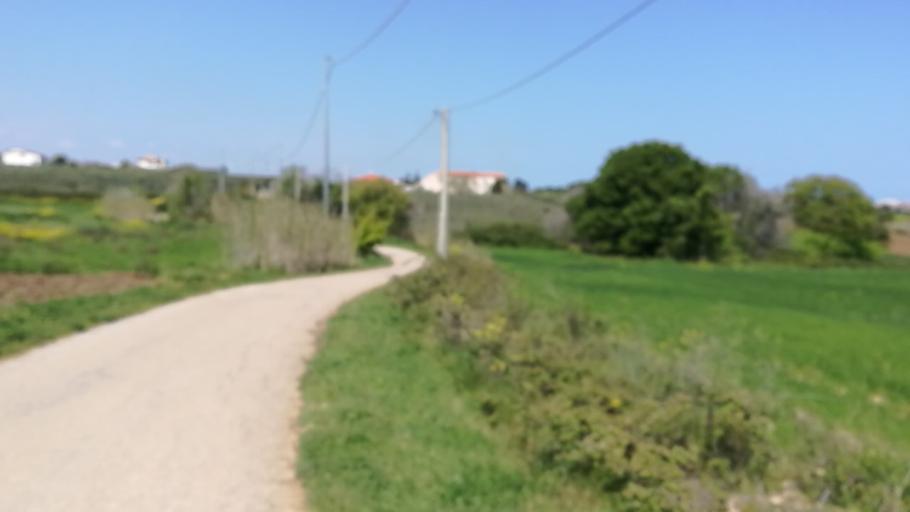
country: IT
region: Molise
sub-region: Provincia di Campobasso
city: Termoli
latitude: 41.9710
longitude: 14.9882
